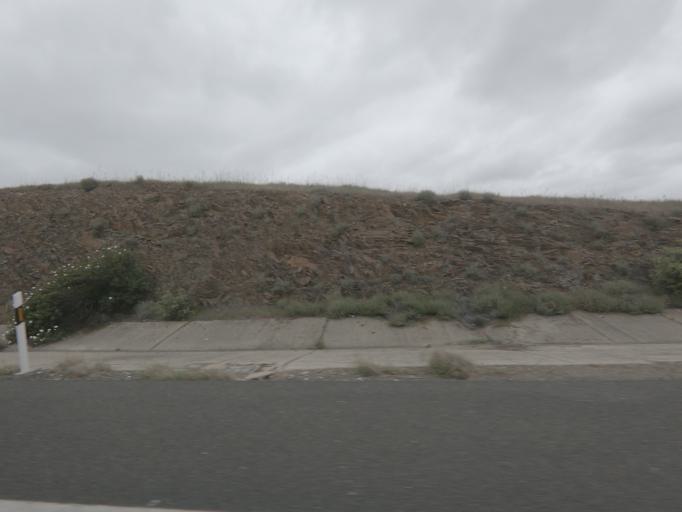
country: ES
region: Extremadura
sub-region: Provincia de Caceres
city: Mirabel
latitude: 39.8924
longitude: -6.2621
